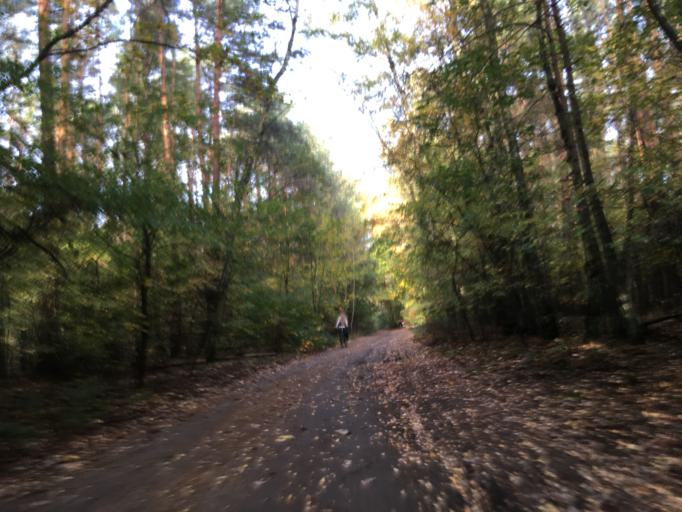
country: DE
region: Brandenburg
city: Glienicke
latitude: 52.6778
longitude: 13.3373
